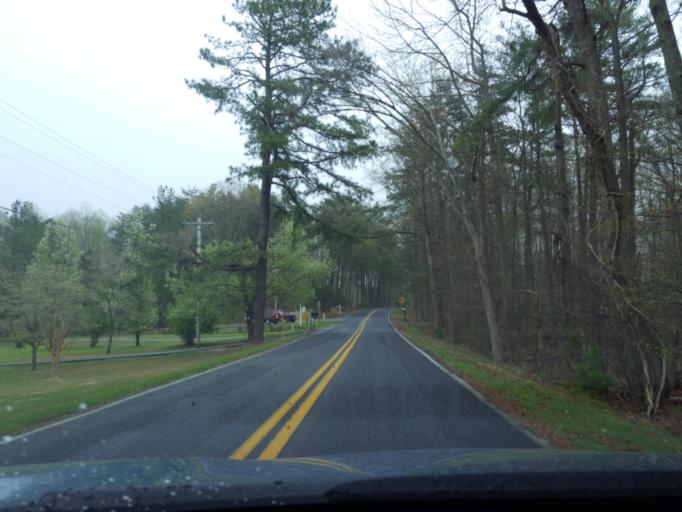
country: US
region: Maryland
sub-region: Saint Mary's County
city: Golden Beach
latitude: 38.5339
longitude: -76.7071
